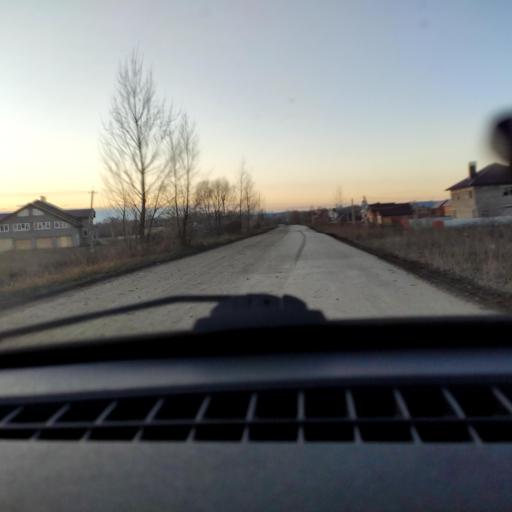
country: RU
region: Bashkortostan
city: Ufa
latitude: 54.7052
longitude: 56.1116
